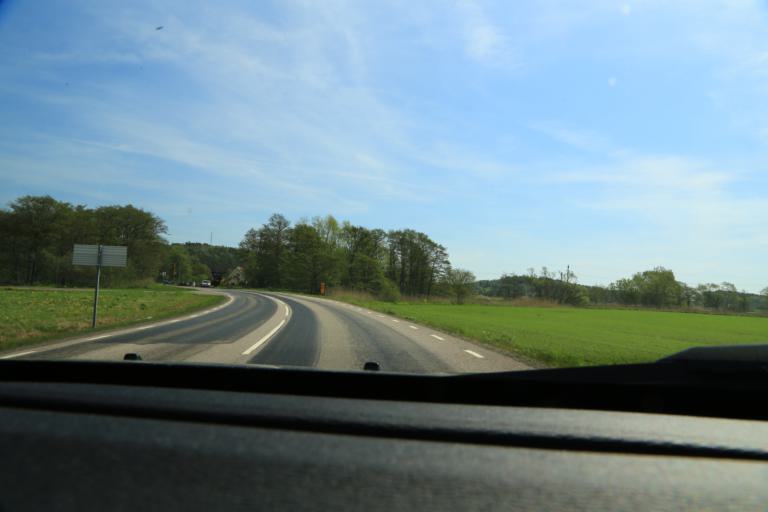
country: SE
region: Halland
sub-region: Varbergs Kommun
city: Varberg
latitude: 57.1451
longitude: 12.2713
